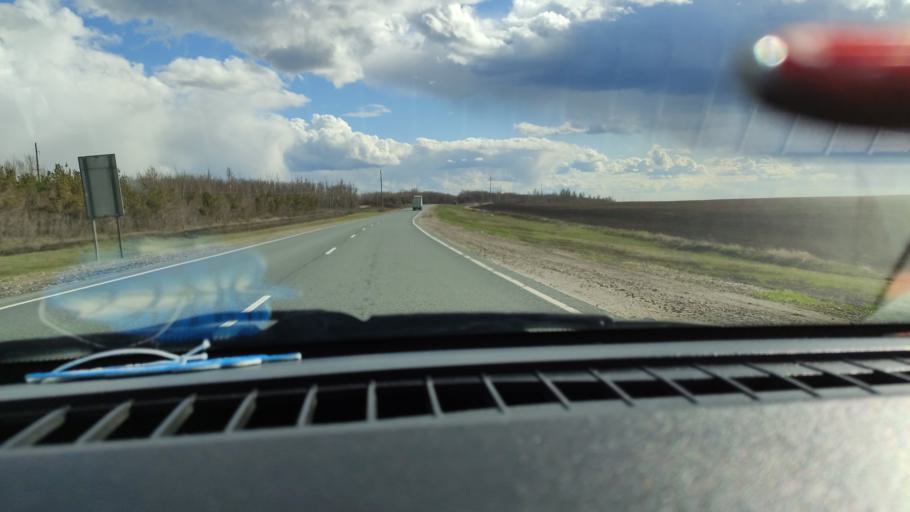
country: RU
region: Saratov
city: Alekseyevka
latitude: 52.2748
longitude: 47.9303
